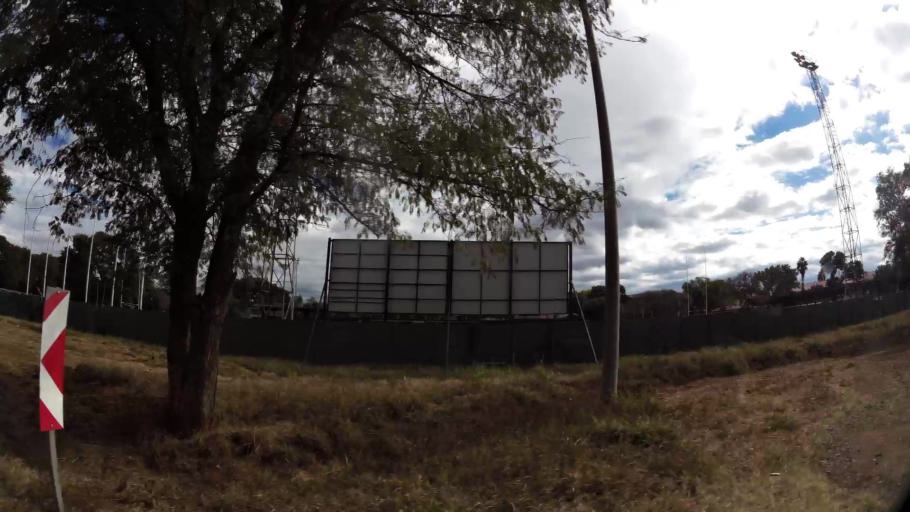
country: ZA
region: Limpopo
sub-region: Waterberg District Municipality
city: Warmbaths
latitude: -24.8896
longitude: 28.2839
